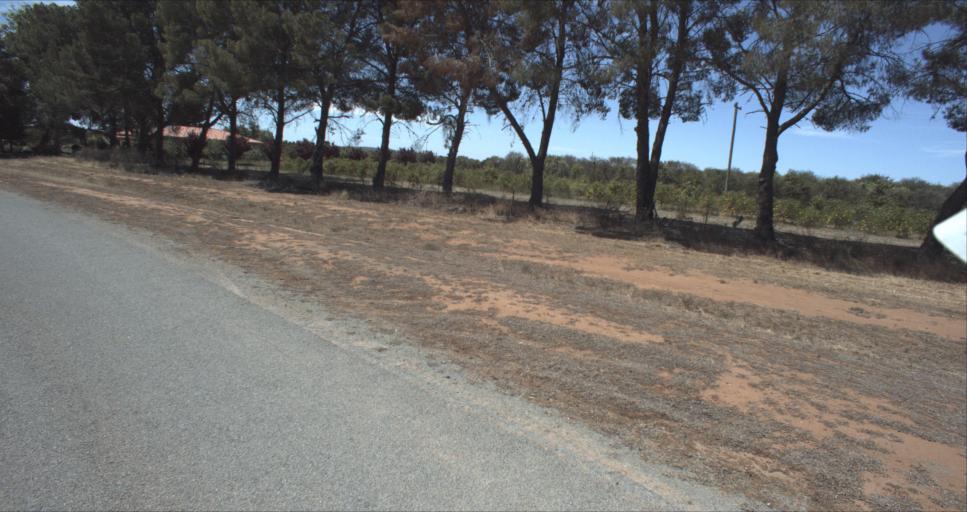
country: AU
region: New South Wales
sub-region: Narrandera
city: Narrandera
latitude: -34.6774
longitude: 146.4408
